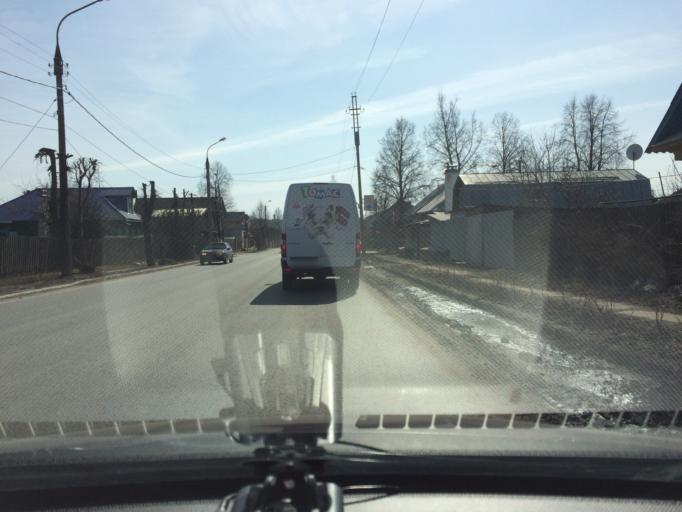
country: RU
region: Mariy-El
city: Yoshkar-Ola
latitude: 56.6470
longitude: 47.9058
